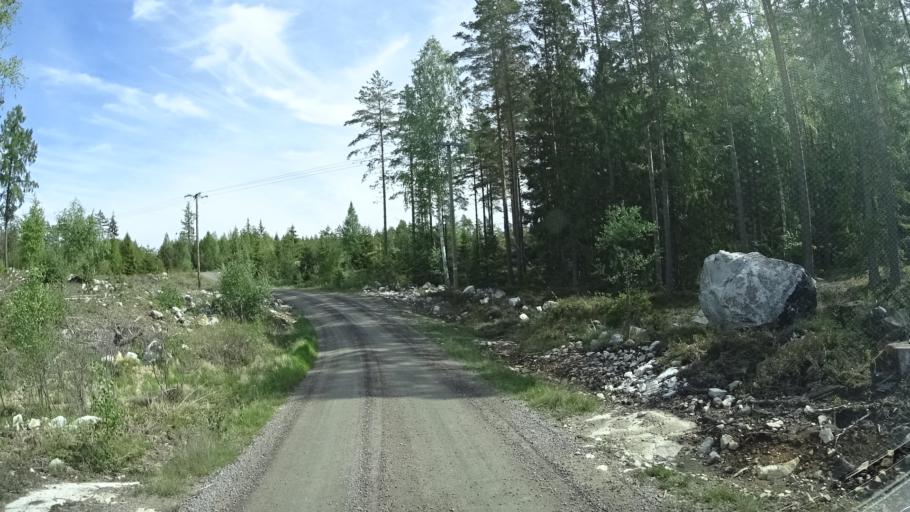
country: SE
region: OEstergoetland
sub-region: Finspangs Kommun
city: Finspang
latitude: 58.7718
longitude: 15.8514
